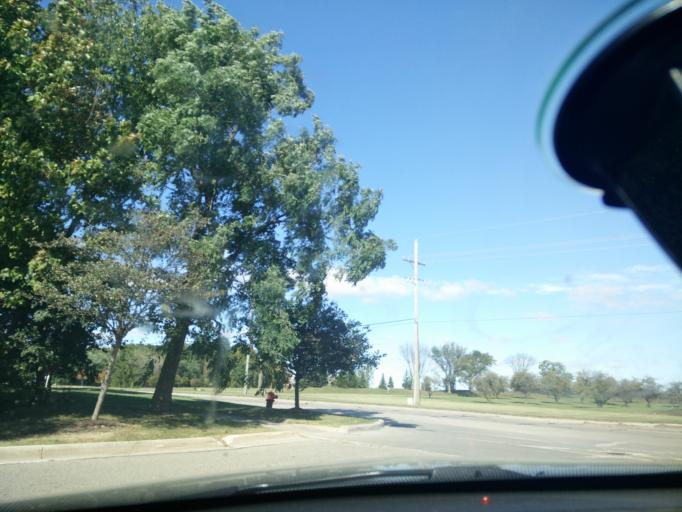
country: US
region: Michigan
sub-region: Wayne County
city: Northville
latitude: 42.3937
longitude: -83.5149
